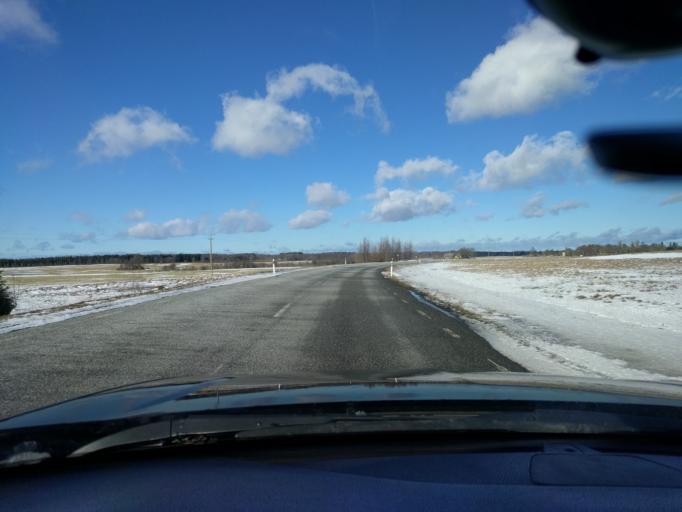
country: EE
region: Harju
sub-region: Raasiku vald
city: Raasiku
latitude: 59.3890
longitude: 25.1901
